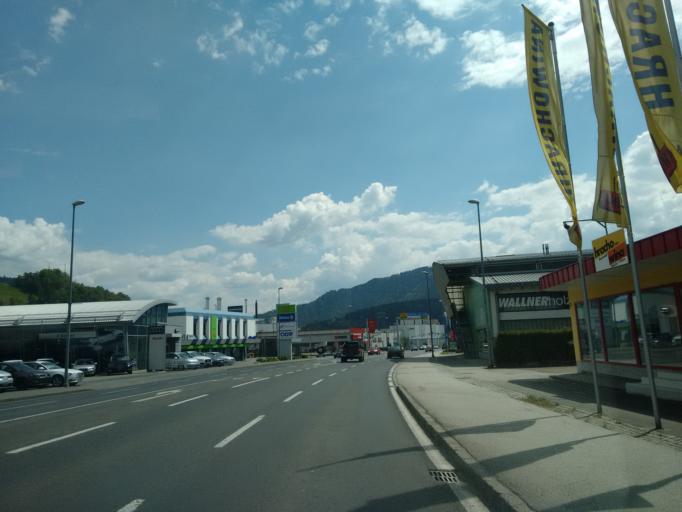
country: AT
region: Styria
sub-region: Politischer Bezirk Bruck-Muerzzuschlag
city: Bruck an der Mur
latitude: 47.4204
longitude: 15.2742
